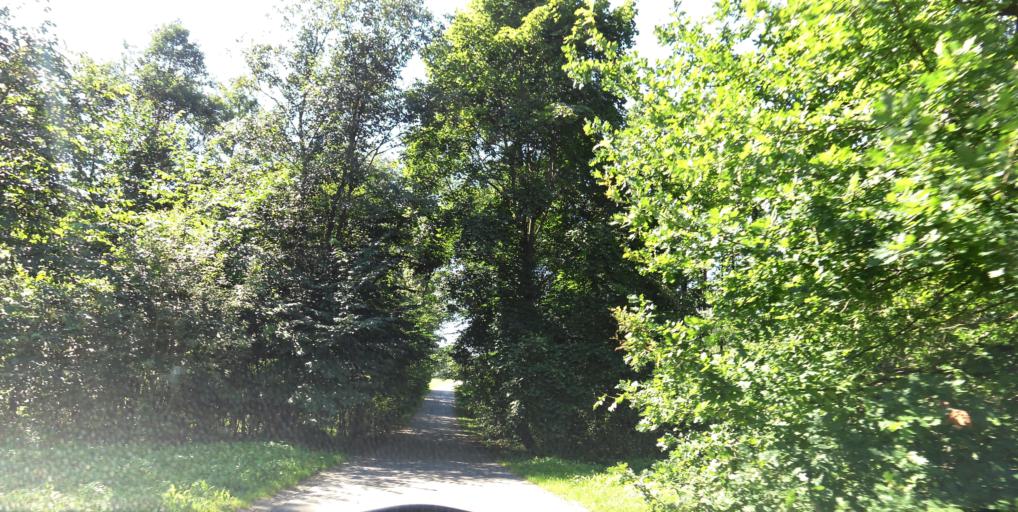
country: LT
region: Vilnius County
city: Rasos
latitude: 54.6888
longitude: 25.3677
